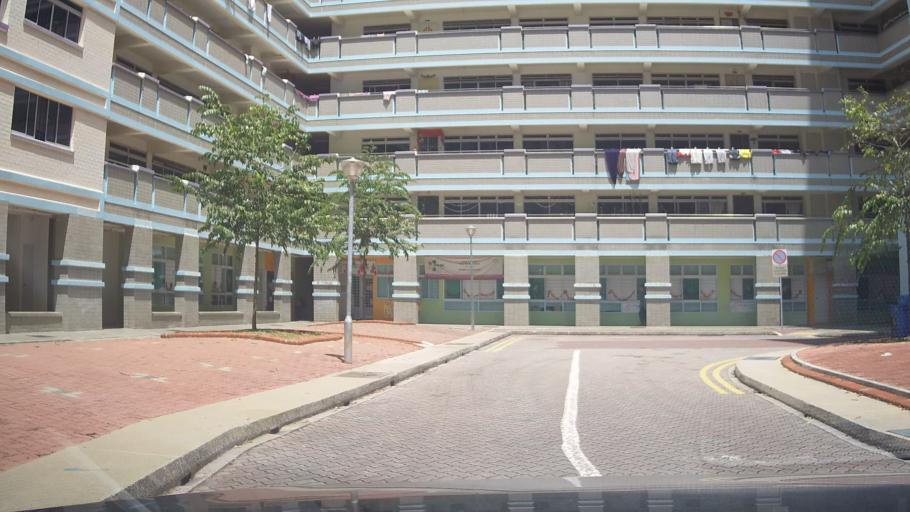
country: MY
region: Johor
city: Kampung Pasir Gudang Baru
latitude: 1.3722
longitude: 103.9615
